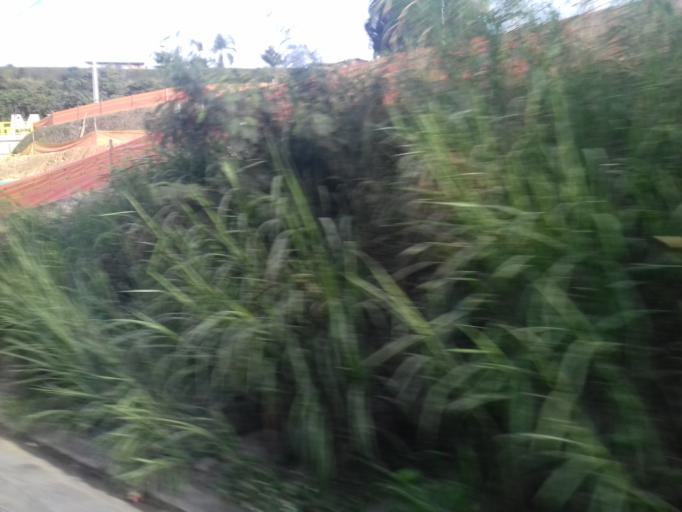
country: CO
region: Antioquia
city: Sabaneta
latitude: 6.1554
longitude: -75.6251
